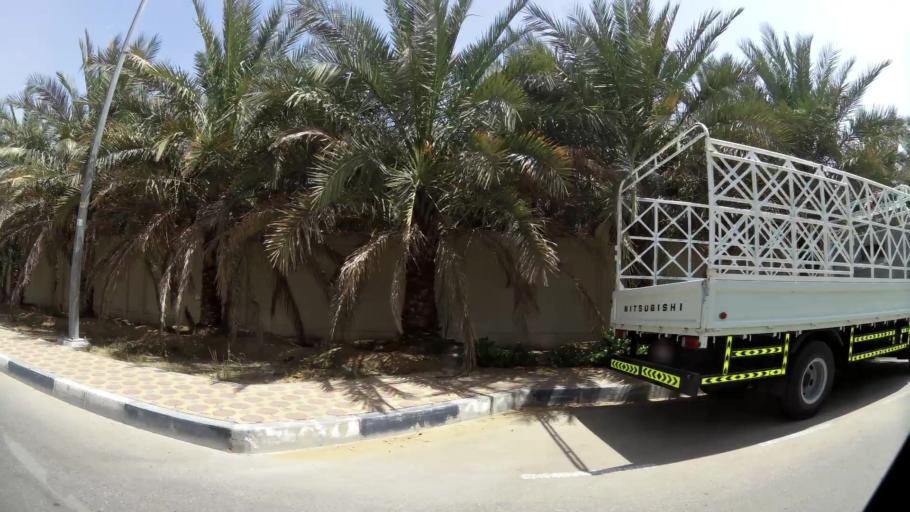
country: AE
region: Abu Dhabi
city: Al Ain
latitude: 24.2578
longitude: 55.6991
